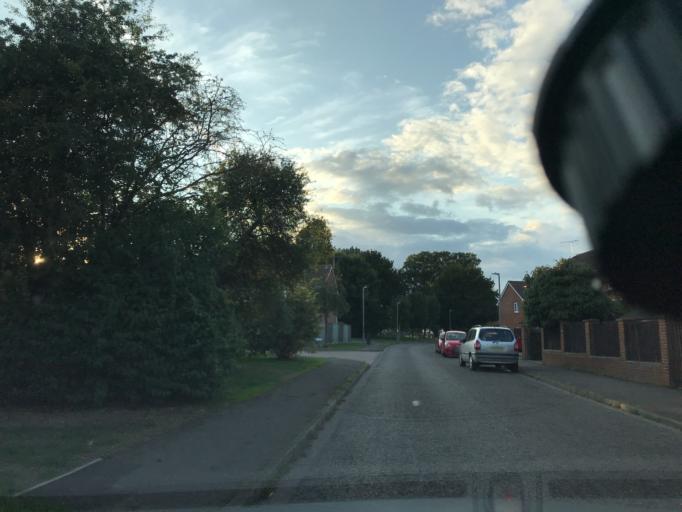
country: GB
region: England
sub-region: Buckinghamshire
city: Aylesbury
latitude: 51.8241
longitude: -0.7936
